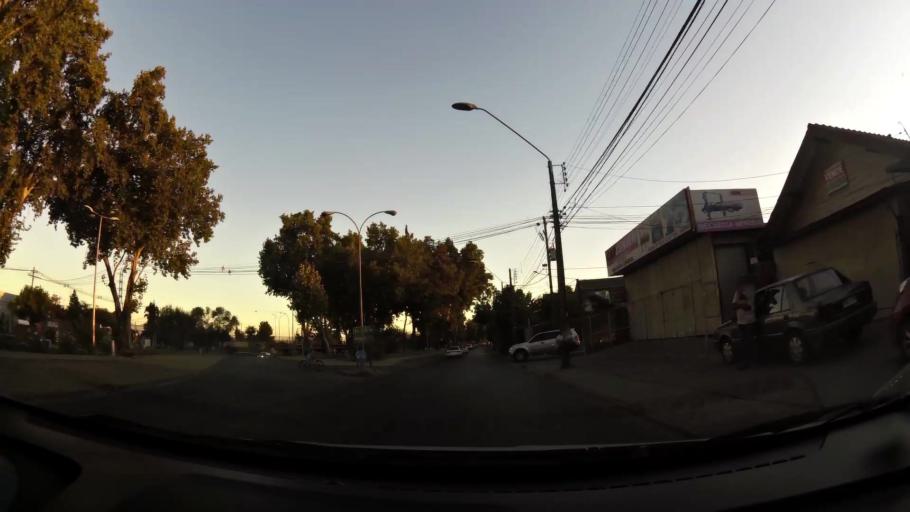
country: CL
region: Maule
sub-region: Provincia de Curico
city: Curico
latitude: -34.9934
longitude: -71.2335
